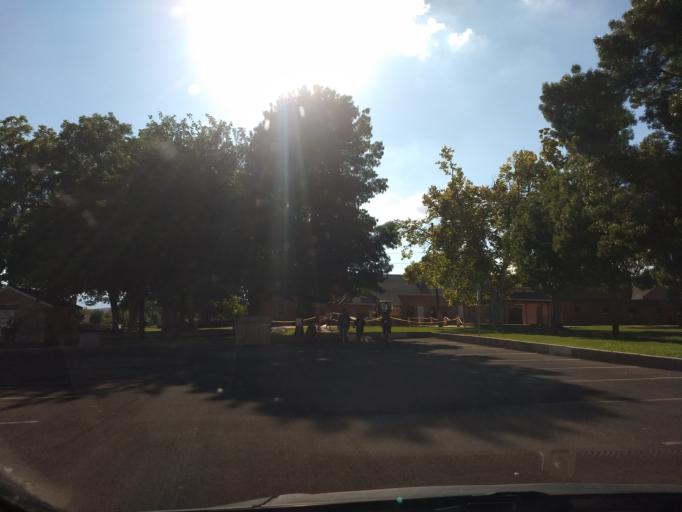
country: US
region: Utah
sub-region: Washington County
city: Washington
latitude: 37.1306
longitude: -113.5084
